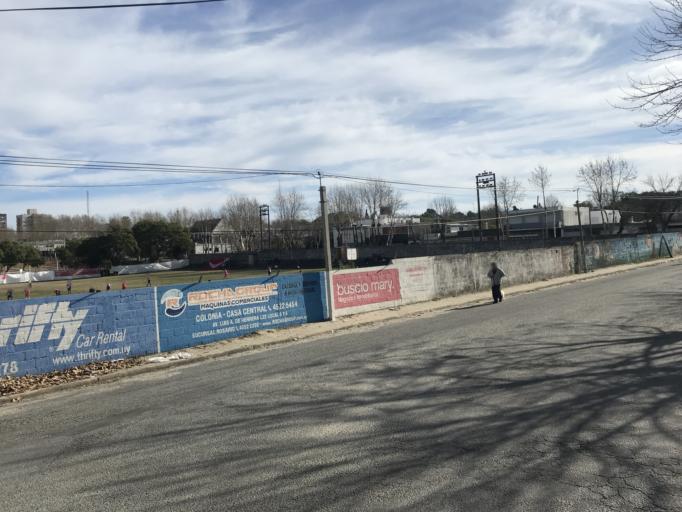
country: UY
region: Colonia
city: Colonia del Sacramento
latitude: -34.4701
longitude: -57.8405
